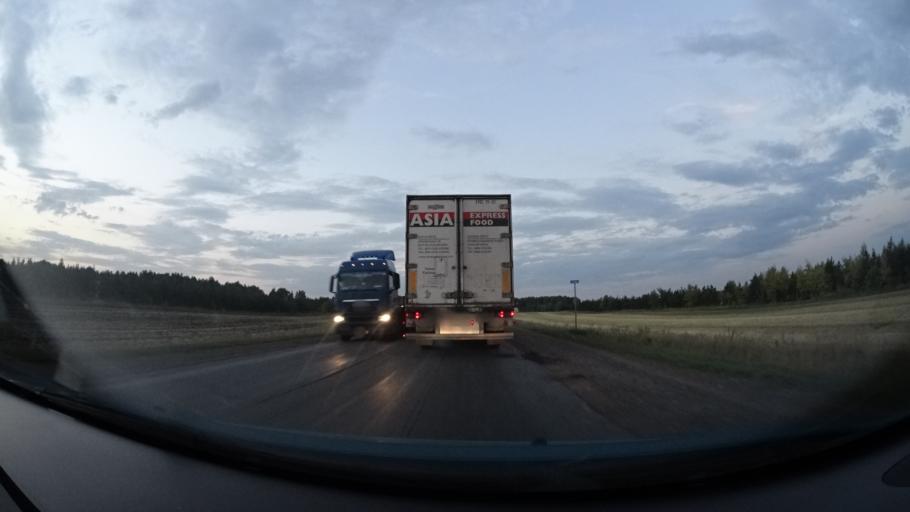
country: RU
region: Tatarstan
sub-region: Bavlinskiy Rayon
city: Bavly
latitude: 54.2822
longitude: 52.9916
